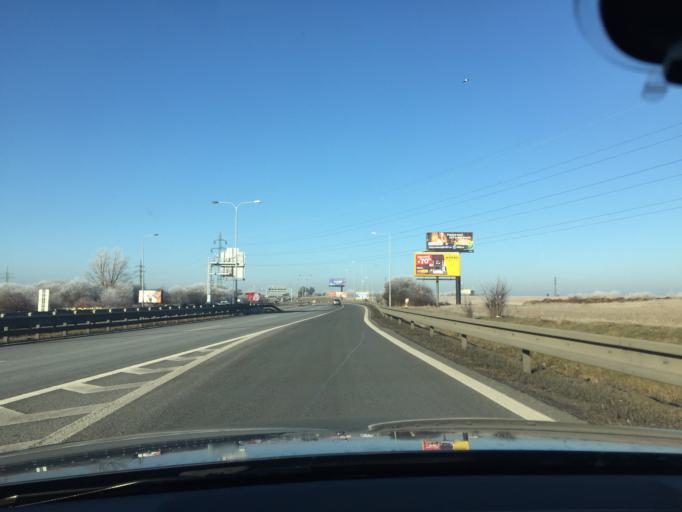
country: CZ
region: Central Bohemia
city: Cernosice
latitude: 50.0163
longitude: 14.3391
